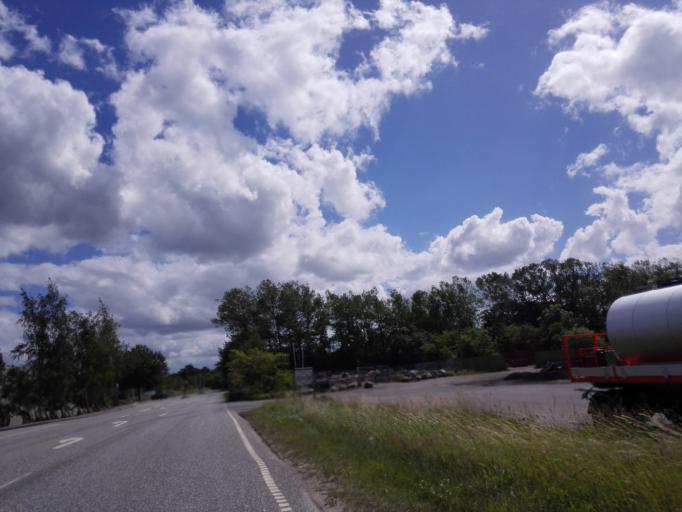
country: DK
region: Capital Region
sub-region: Allerod Kommune
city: Lynge
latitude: 55.8266
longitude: 12.3020
